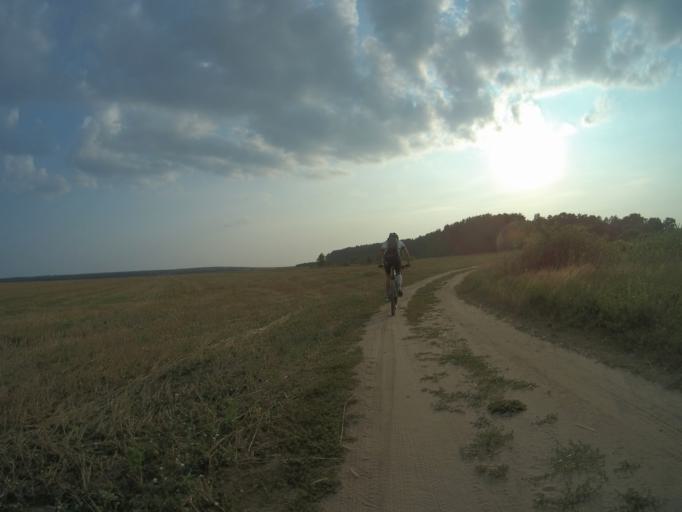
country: RU
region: Vladimir
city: Orgtrud
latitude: 56.2962
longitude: 40.6190
